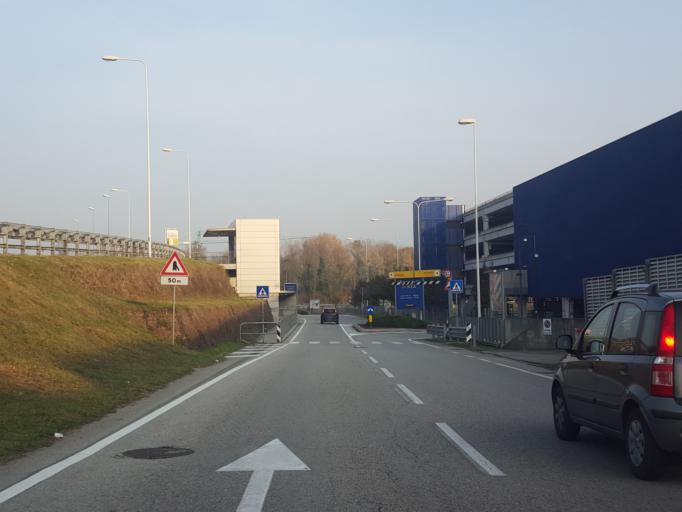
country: IT
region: Veneto
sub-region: Provincia di Padova
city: Noventa
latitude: 45.4198
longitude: 11.9333
